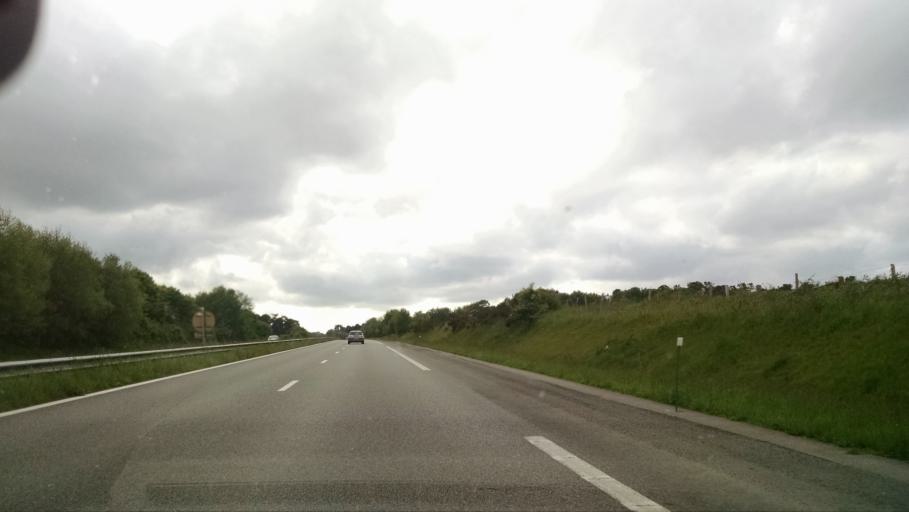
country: FR
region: Brittany
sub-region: Departement du Finistere
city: Plouigneau
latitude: 48.5812
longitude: -3.7477
